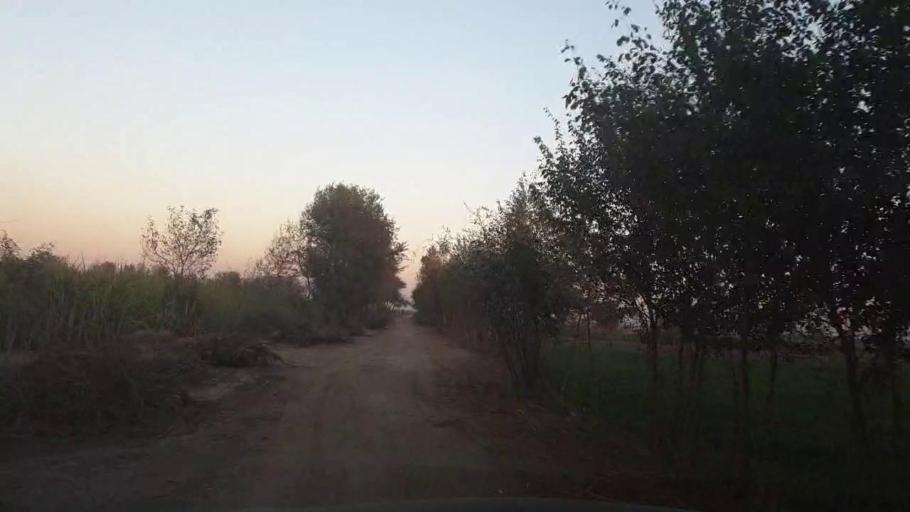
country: PK
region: Sindh
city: Ghotki
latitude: 28.0107
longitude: 69.3796
